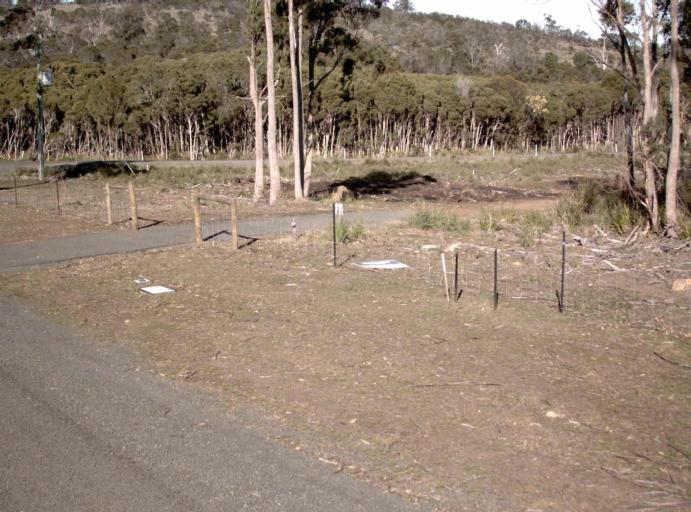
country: AU
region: Tasmania
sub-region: Launceston
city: Mayfield
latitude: -41.2816
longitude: 147.0288
